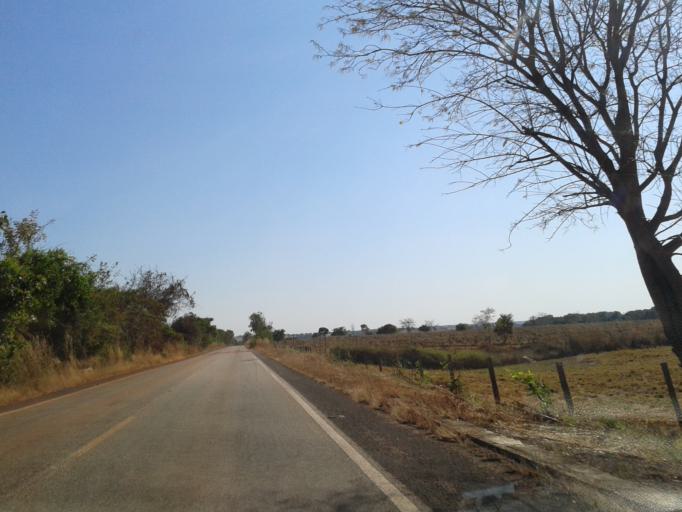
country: BR
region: Goias
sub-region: Mozarlandia
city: Mozarlandia
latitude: -14.6292
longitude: -50.5189
